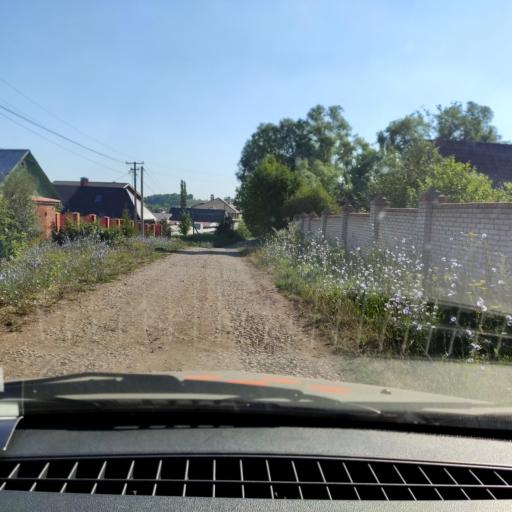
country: RU
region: Bashkortostan
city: Avdon
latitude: 54.5921
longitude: 55.7035
